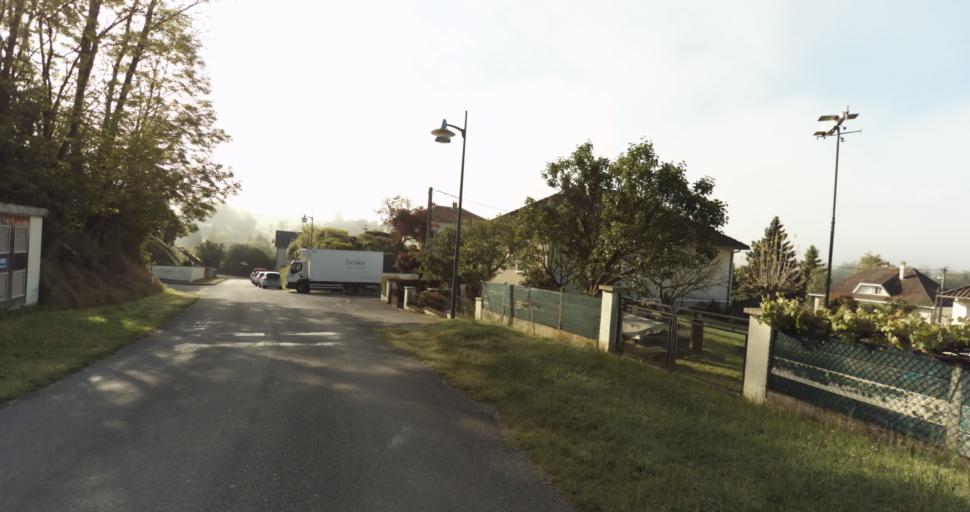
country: FR
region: Limousin
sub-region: Departement de la Haute-Vienne
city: Le Vigen
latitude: 45.7523
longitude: 1.2883
